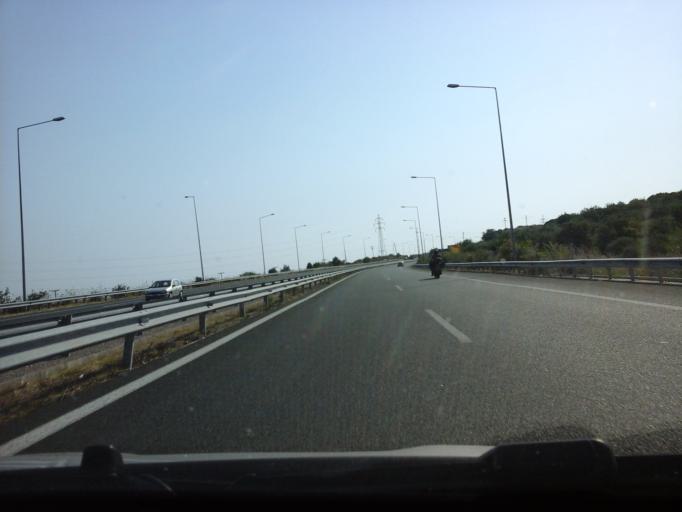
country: GR
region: East Macedonia and Thrace
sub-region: Nomos Evrou
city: Alexandroupoli
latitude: 40.8619
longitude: 25.7593
